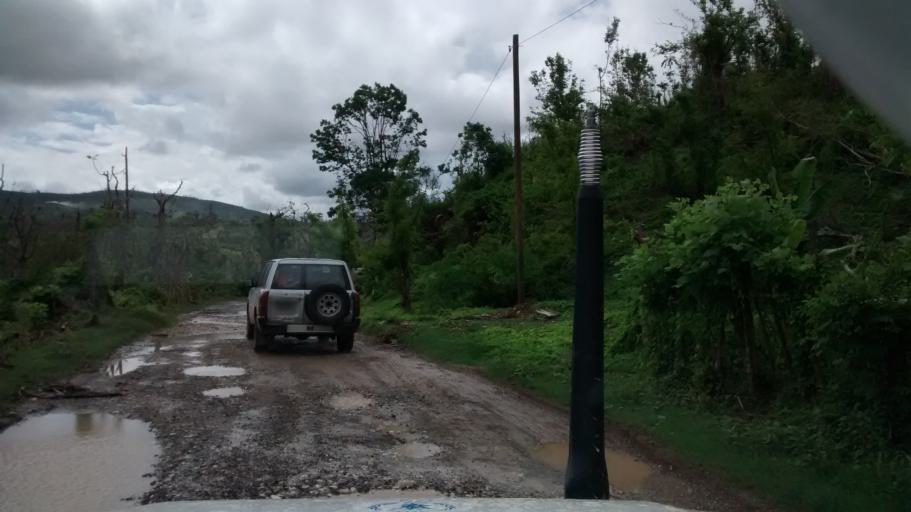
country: HT
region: Grandans
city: Jeremie
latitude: 18.5974
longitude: -74.1801
